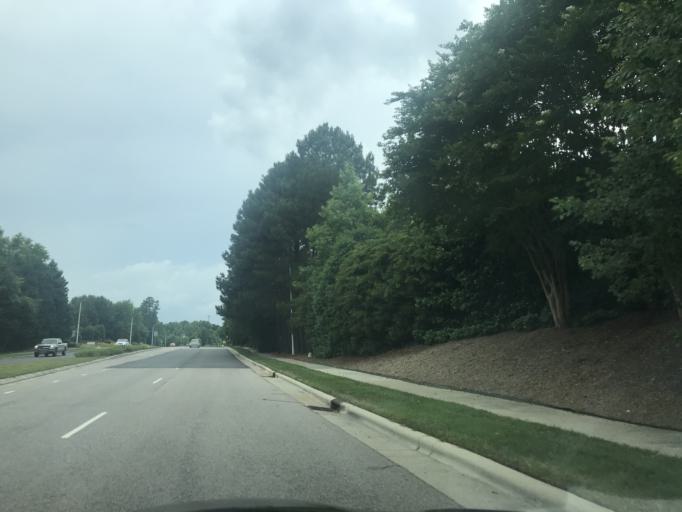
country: US
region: North Carolina
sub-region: Wake County
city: Morrisville
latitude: 35.8140
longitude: -78.8585
